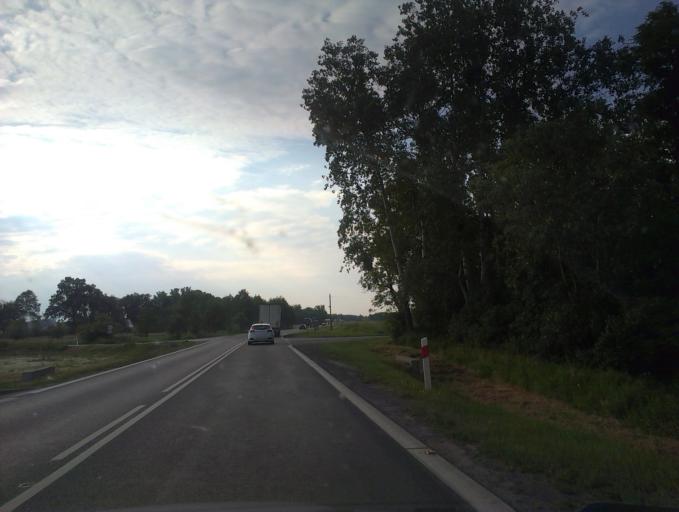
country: PL
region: Lower Silesian Voivodeship
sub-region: Powiat trzebnicki
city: Prusice
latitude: 51.3845
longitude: 16.9413
